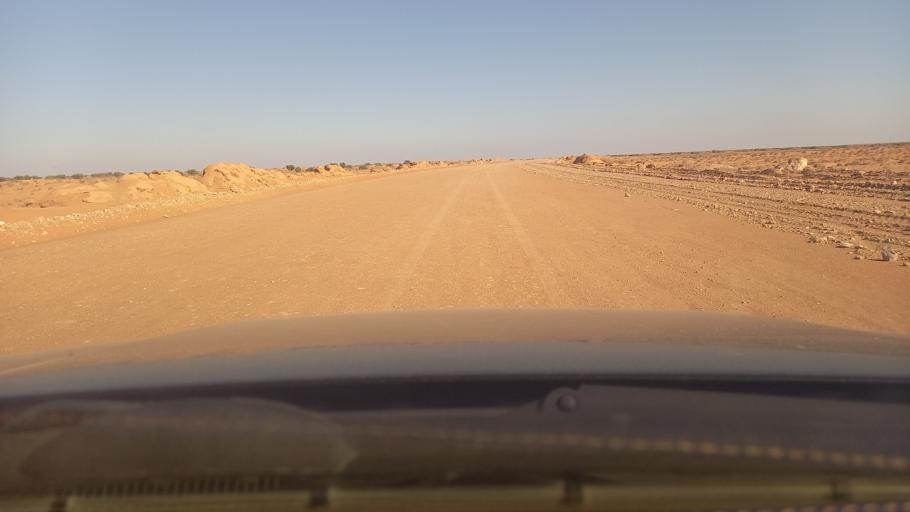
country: TN
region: Madanin
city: Medenine
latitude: 33.1503
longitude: 10.5086
